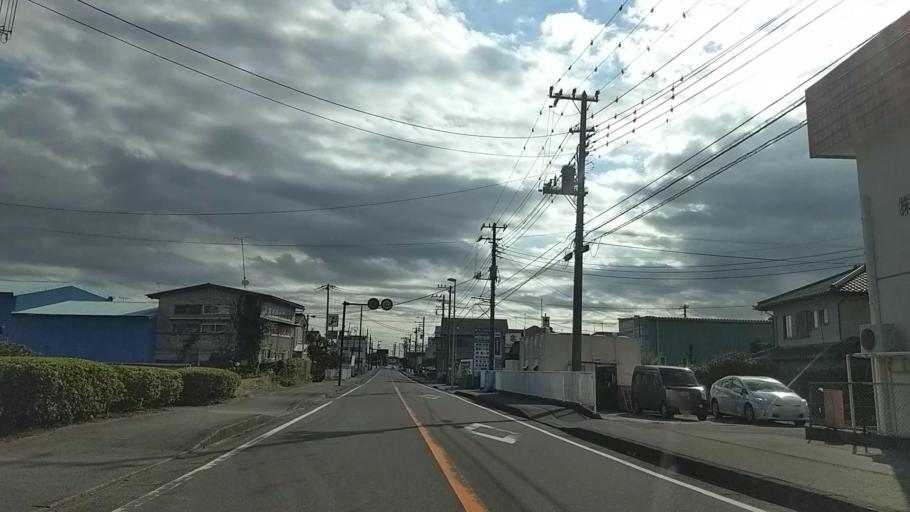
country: JP
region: Kanagawa
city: Ninomiya
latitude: 35.2872
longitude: 139.2044
